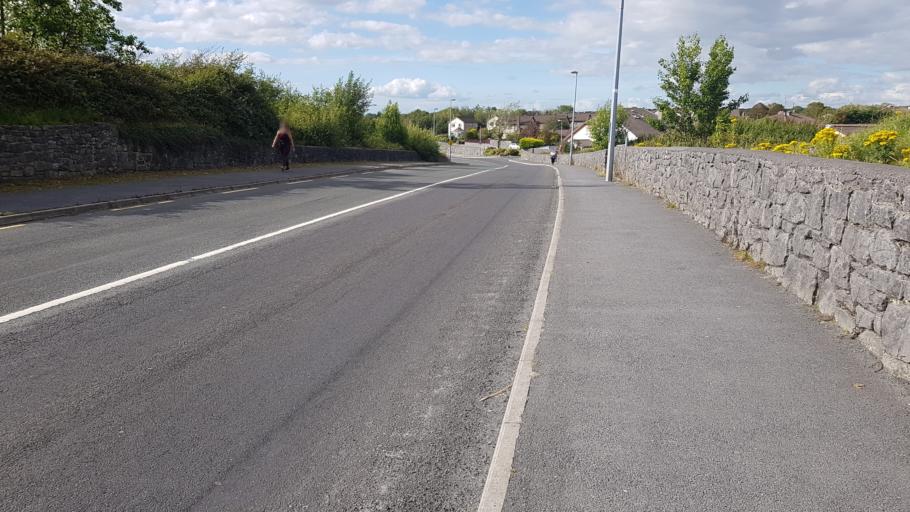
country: IE
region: Connaught
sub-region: County Galway
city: Gaillimh
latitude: 53.2908
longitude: -9.0514
